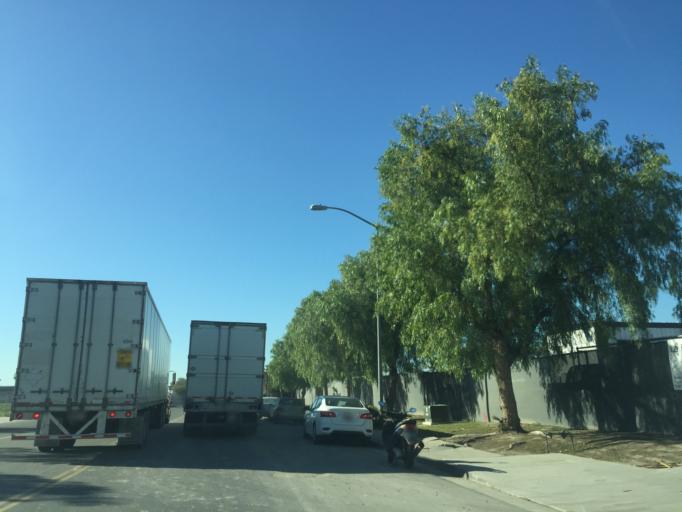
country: MX
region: Baja California
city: Tijuana
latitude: 32.5529
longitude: -116.9306
